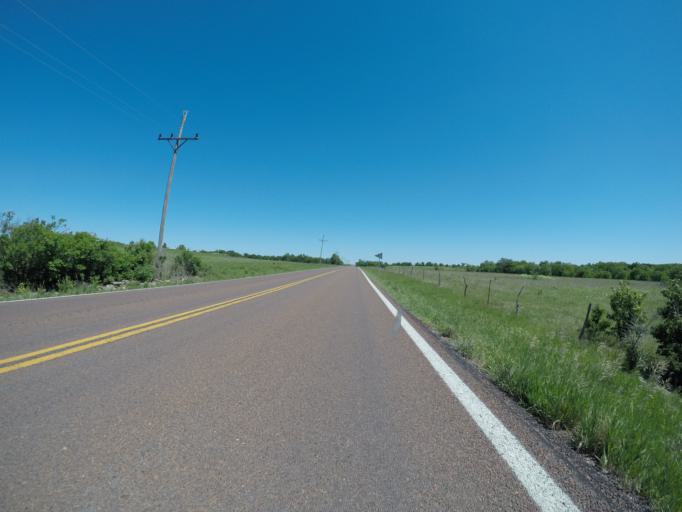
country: US
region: Kansas
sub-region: Wabaunsee County
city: Alma
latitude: 38.8816
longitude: -96.0857
